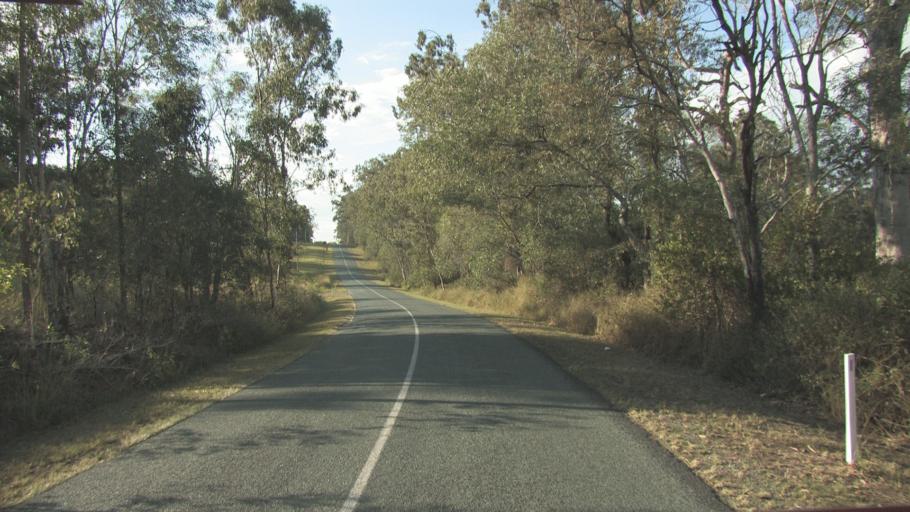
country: AU
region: Queensland
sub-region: Gold Coast
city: Ormeau Hills
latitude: -27.8372
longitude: 153.1685
